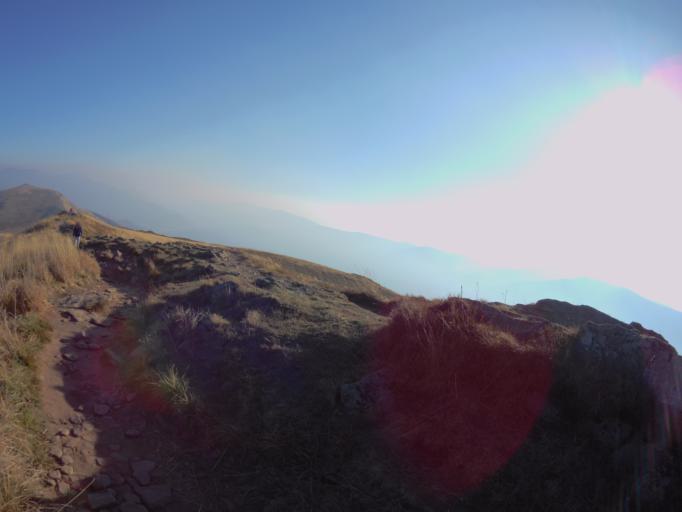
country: PL
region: Subcarpathian Voivodeship
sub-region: Powiat bieszczadzki
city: Lutowiska
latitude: 49.1376
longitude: 22.6047
